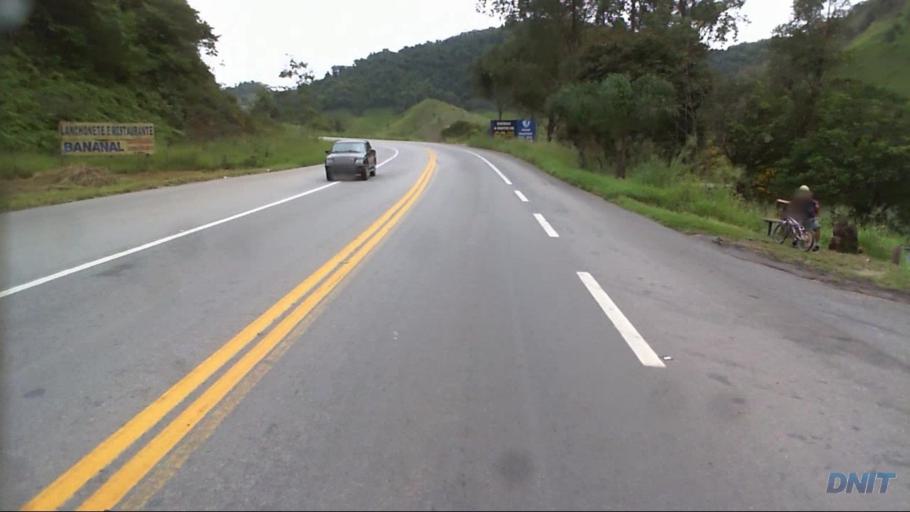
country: BR
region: Minas Gerais
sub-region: Timoteo
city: Timoteo
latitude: -19.6275
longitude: -42.8338
